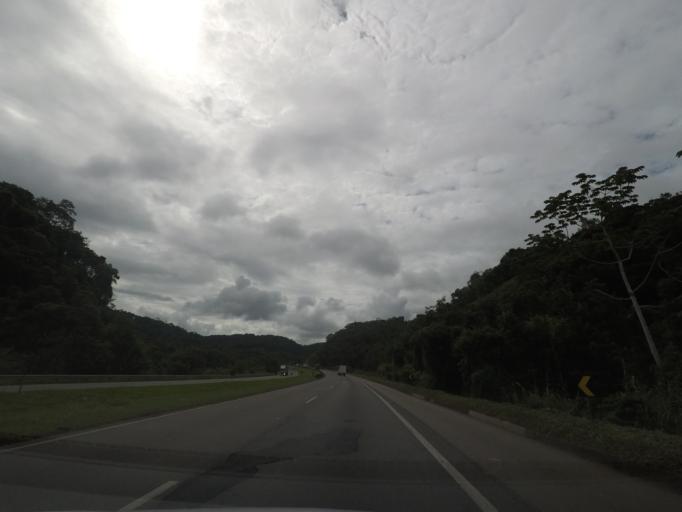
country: BR
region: Sao Paulo
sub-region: Miracatu
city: Miracatu
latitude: -24.2379
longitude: -47.3610
